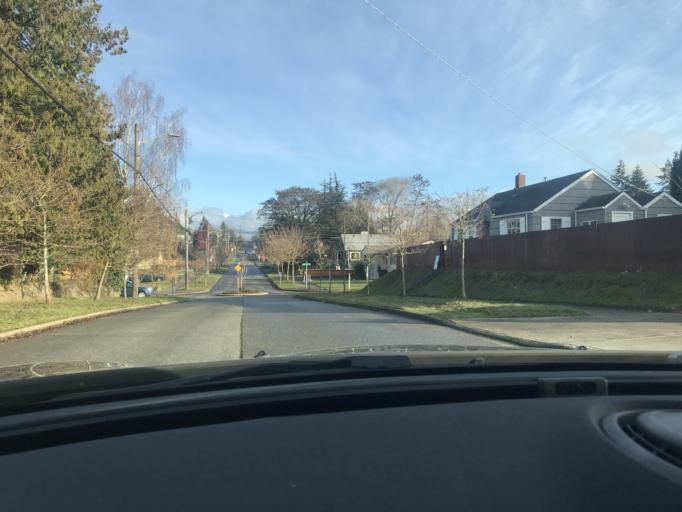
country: US
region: Washington
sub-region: King County
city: White Center
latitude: 47.5247
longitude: -122.3586
